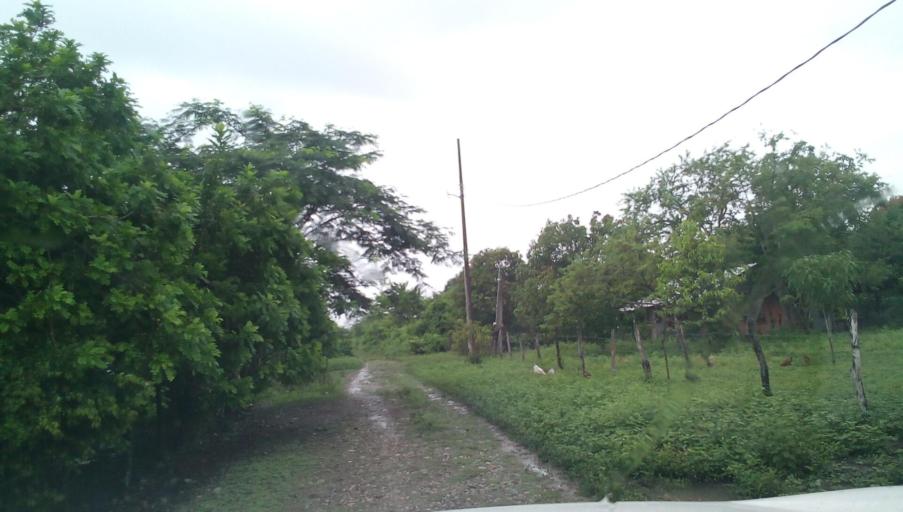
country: MX
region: Veracruz
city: Tempoal de Sanchez
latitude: 21.4194
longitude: -98.4322
